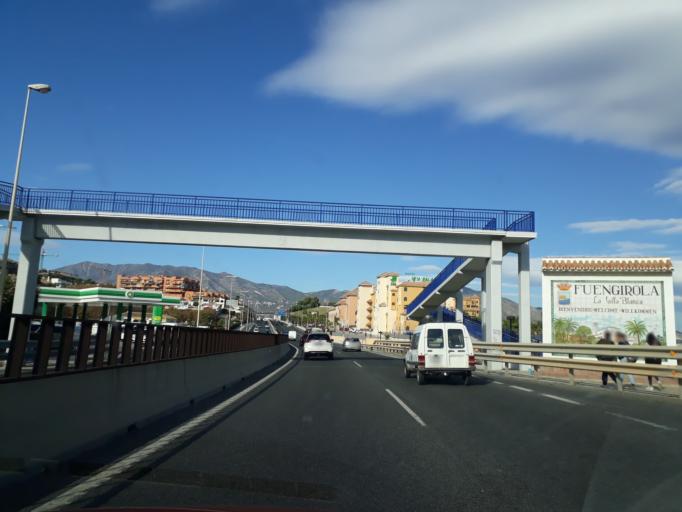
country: ES
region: Andalusia
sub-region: Provincia de Malaga
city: Fuengirola
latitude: 36.5224
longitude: -4.6301
